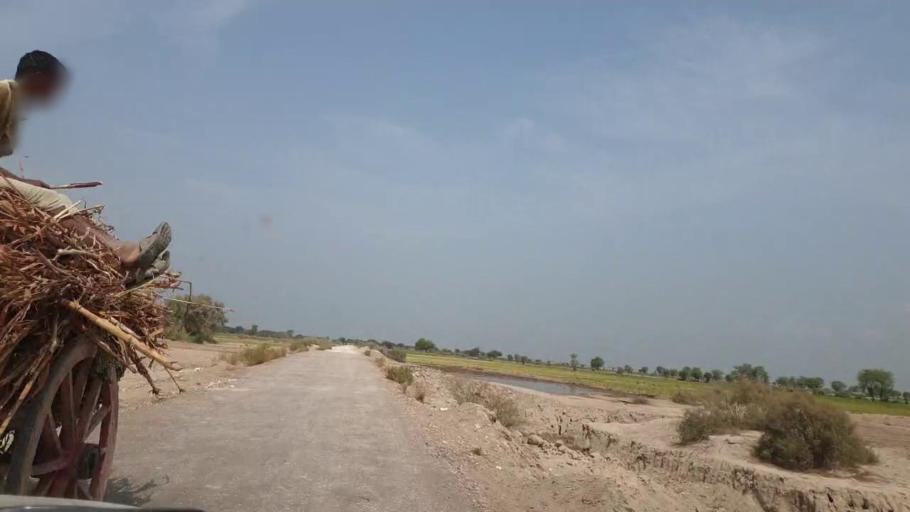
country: PK
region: Sindh
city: Dokri
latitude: 27.3988
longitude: 68.2553
